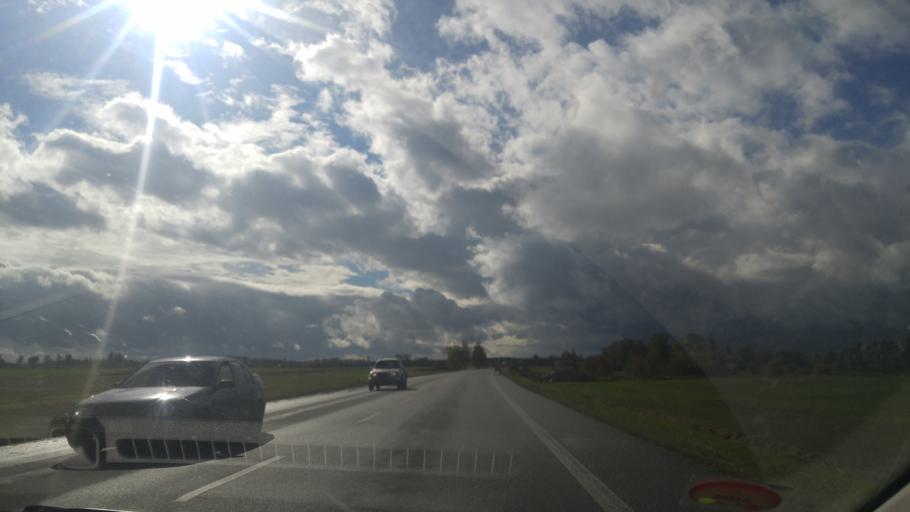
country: CZ
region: Jihocesky
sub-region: Okres Tabor
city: Veseli nad Luznici
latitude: 49.1775
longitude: 14.6888
